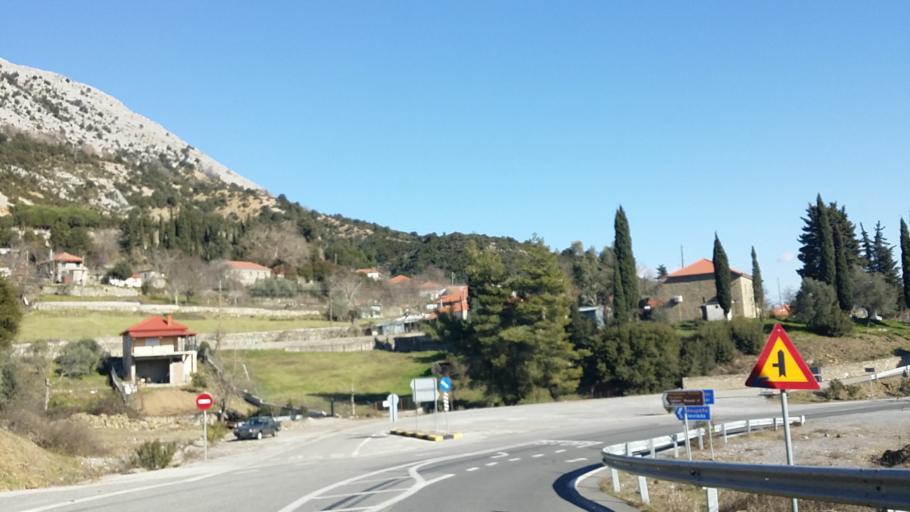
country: GR
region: Central Greece
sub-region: Nomos Evrytanias
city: Kerasochori
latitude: 38.9278
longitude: 21.4354
